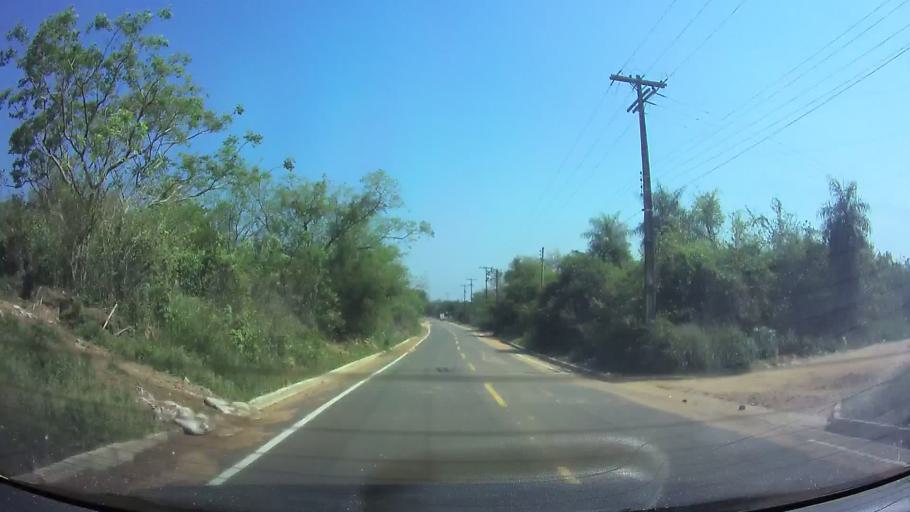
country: PY
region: Central
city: Limpio
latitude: -25.2196
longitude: -57.4850
